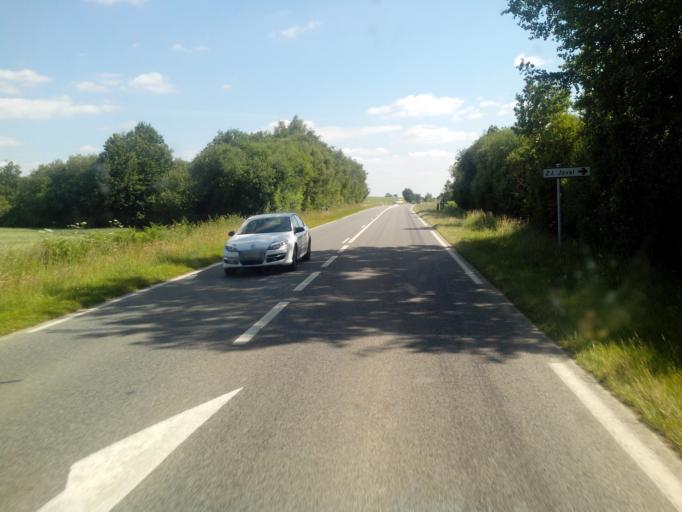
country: FR
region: Brittany
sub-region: Departement d'Ille-et-Vilaine
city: Acigne
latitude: 48.1409
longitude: -1.5164
